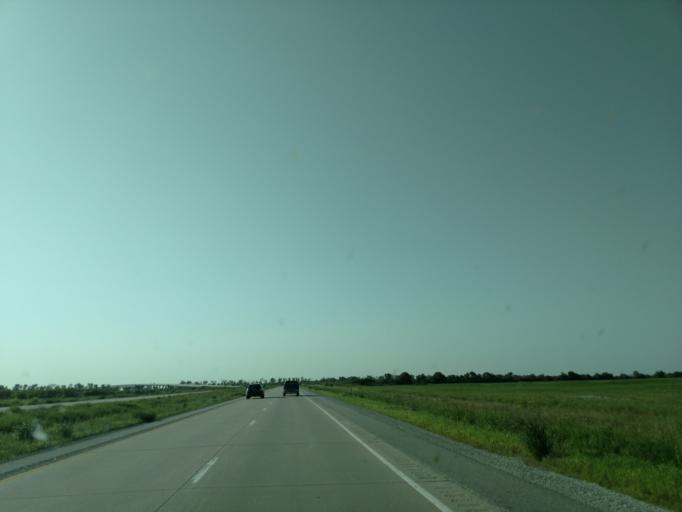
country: US
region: Nebraska
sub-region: Cass County
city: Plattsmouth
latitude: 41.0553
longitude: -95.8657
